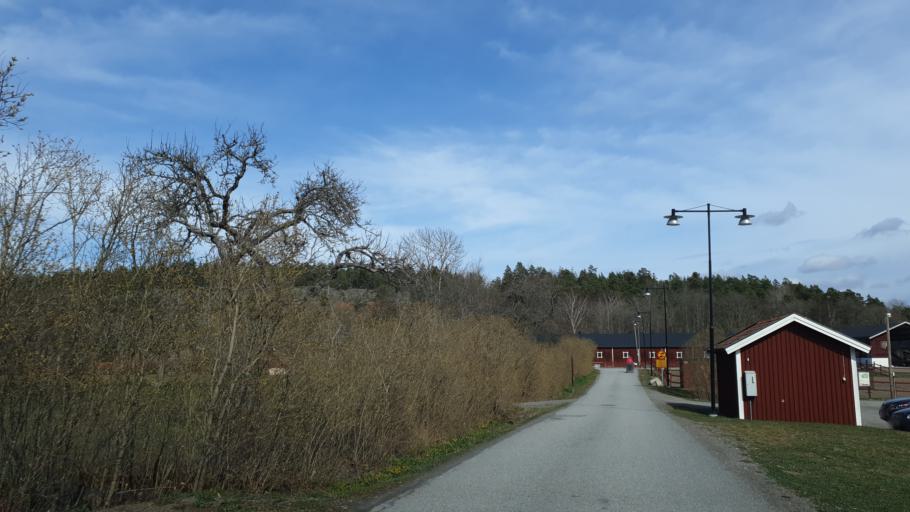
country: SE
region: Stockholm
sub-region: Nacka Kommun
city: Kummelnas
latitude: 59.3459
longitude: 18.3231
